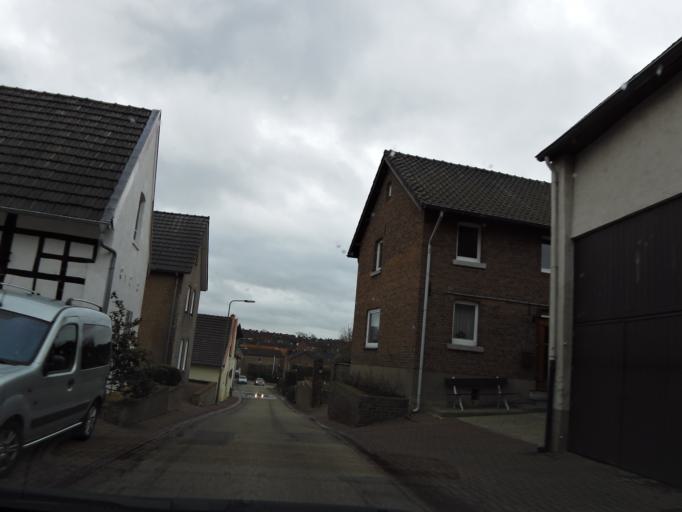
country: NL
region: Limburg
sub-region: Eijsden-Margraten
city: Margraten
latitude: 50.7932
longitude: 5.8060
